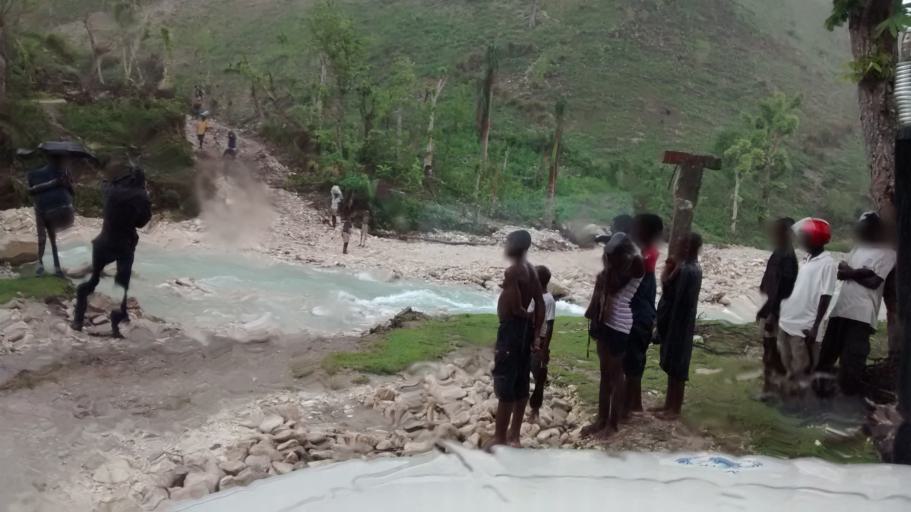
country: HT
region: Grandans
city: Moron
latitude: 18.5376
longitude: -74.1762
